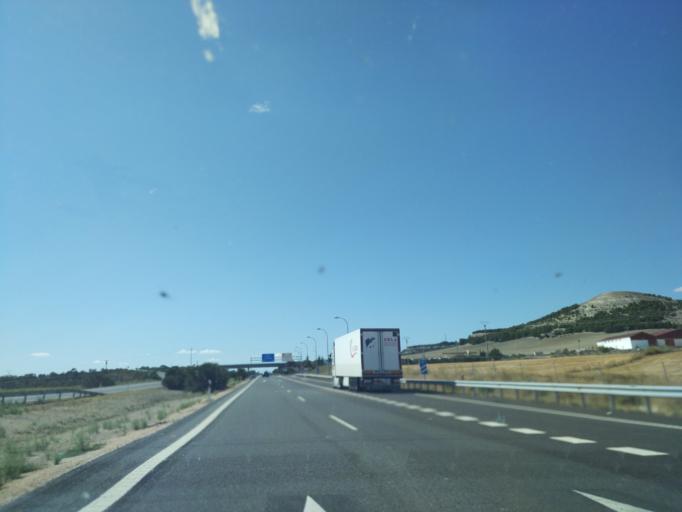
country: ES
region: Castille and Leon
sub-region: Provincia de Valladolid
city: Tordesillas
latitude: 41.5224
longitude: -5.0387
